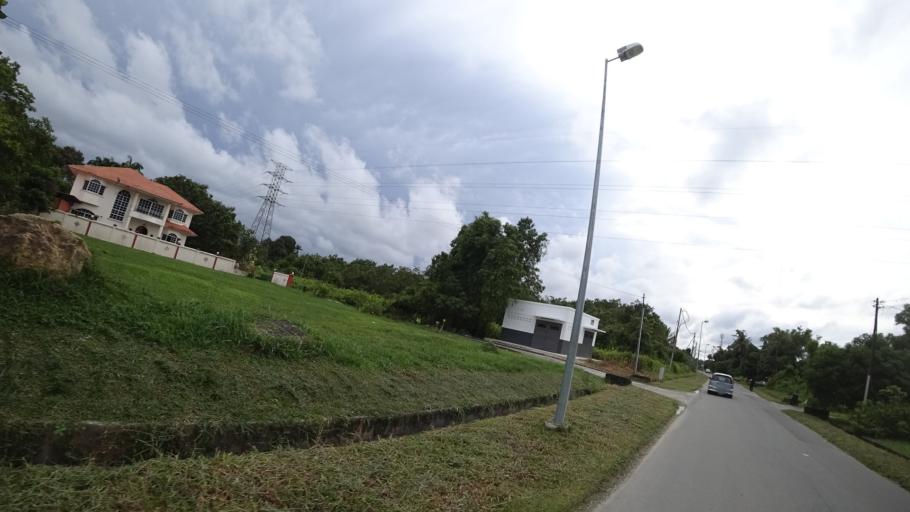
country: BN
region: Brunei and Muara
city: Bandar Seri Begawan
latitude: 4.8590
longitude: 114.8600
